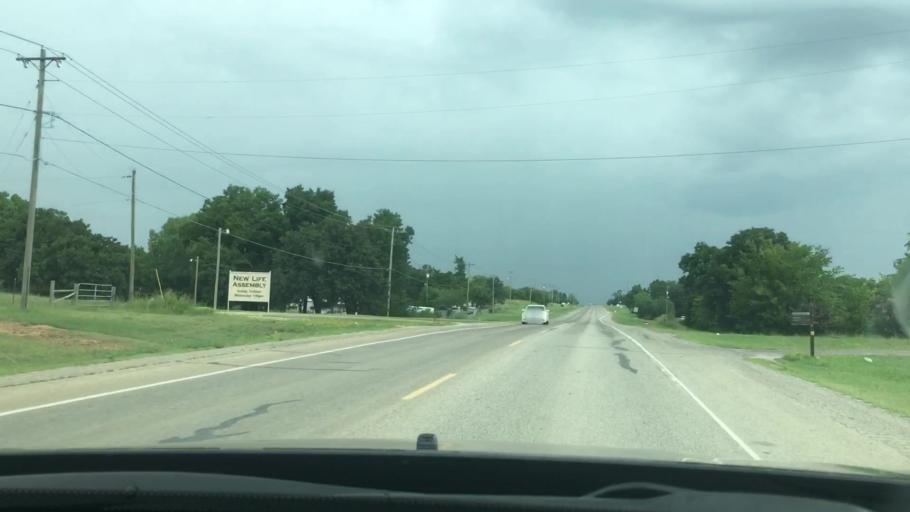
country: US
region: Oklahoma
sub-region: Carter County
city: Healdton
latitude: 34.2087
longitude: -97.4747
